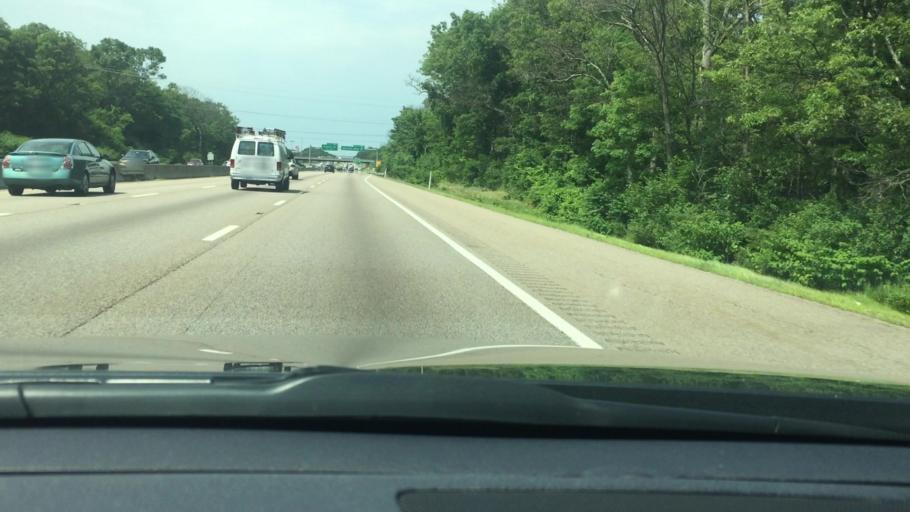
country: US
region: Massachusetts
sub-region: Norfolk County
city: Avon
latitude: 42.1198
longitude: -71.0610
